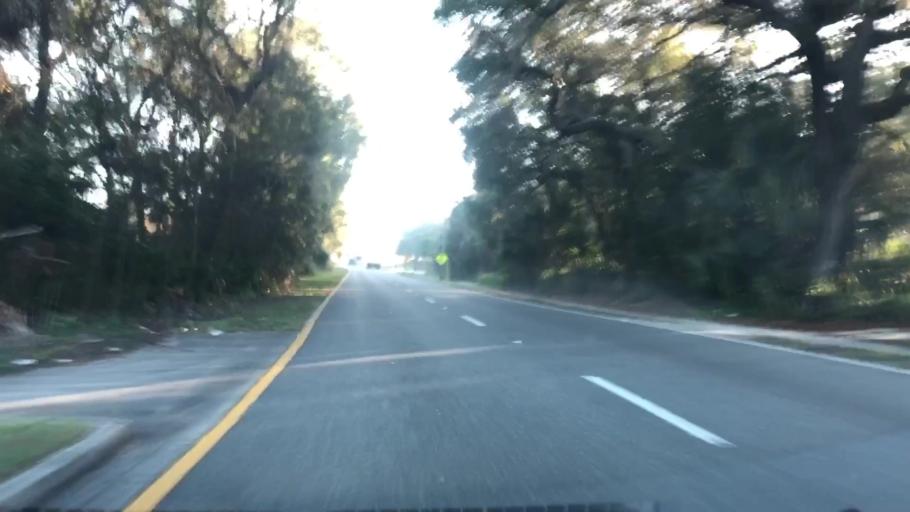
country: US
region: Florida
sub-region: Seminole County
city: Lake Mary
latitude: 28.7856
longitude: -81.3427
